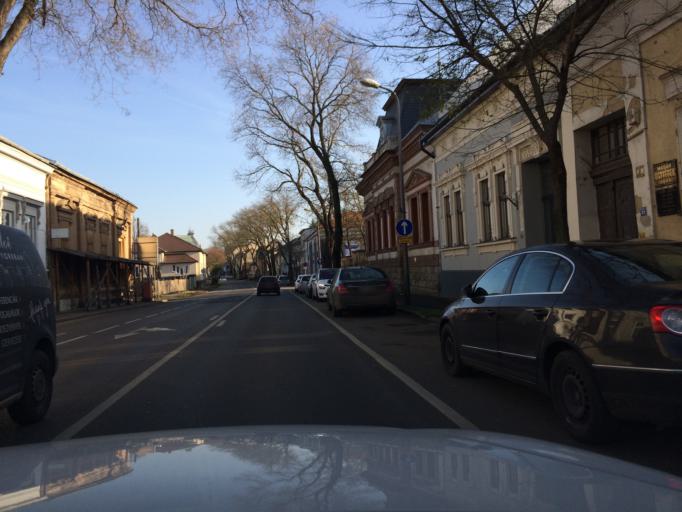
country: HU
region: Szabolcs-Szatmar-Bereg
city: Nyiregyhaza
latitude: 47.9542
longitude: 21.7212
